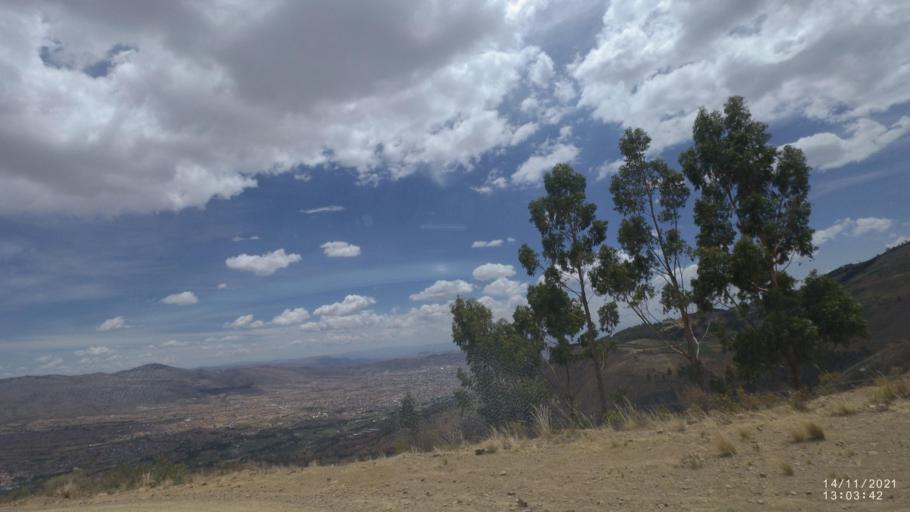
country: BO
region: Cochabamba
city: Colomi
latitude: -17.3700
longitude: -65.9785
